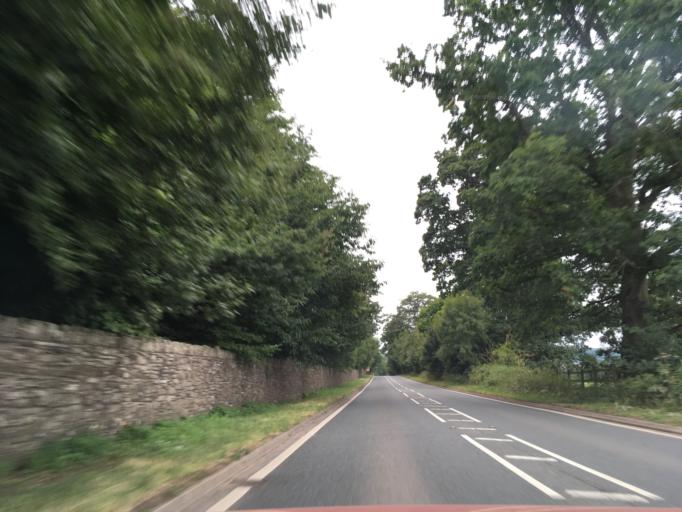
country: GB
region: Wales
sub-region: Blaenau Gwent
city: Brynmawr
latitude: 51.8748
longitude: -3.1790
